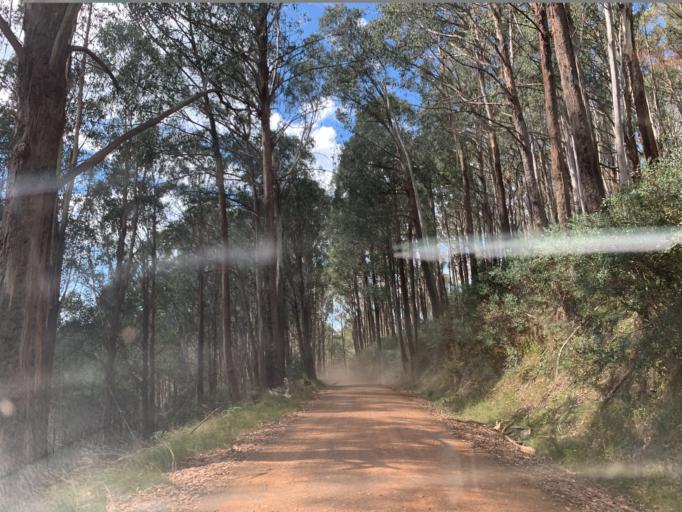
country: AU
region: Victoria
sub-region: Mansfield
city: Mansfield
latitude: -37.0973
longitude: 146.5387
